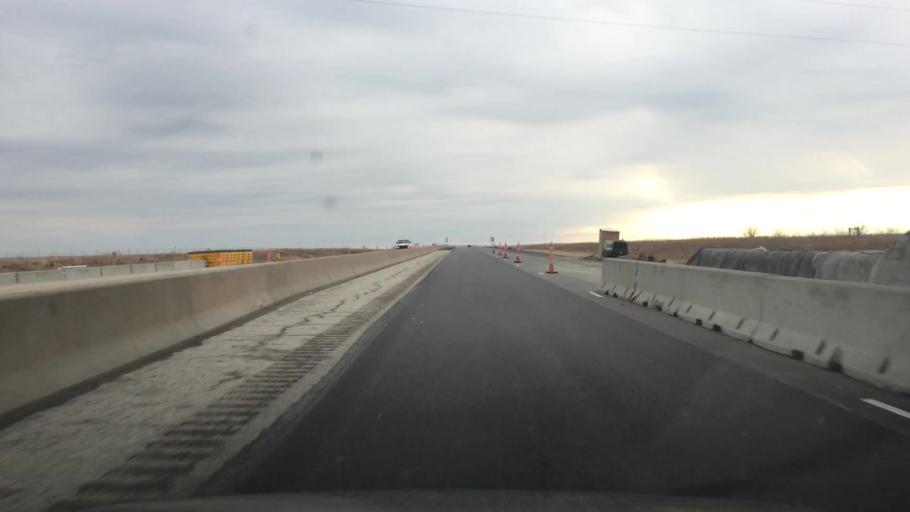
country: US
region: Kansas
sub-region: Osage County
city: Osage City
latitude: 38.6952
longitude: -95.9930
